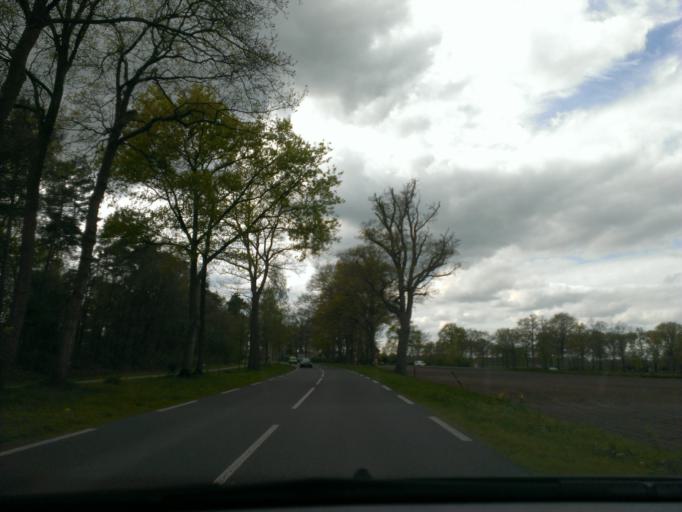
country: NL
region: Overijssel
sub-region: Gemeente Borne
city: Borne
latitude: 52.3140
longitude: 6.6973
